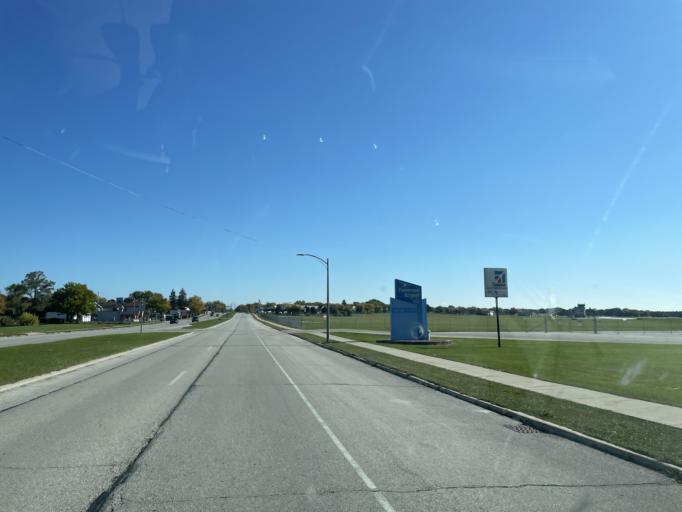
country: US
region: Wisconsin
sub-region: Waukesha County
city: Butler
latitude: 43.1161
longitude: -88.0305
